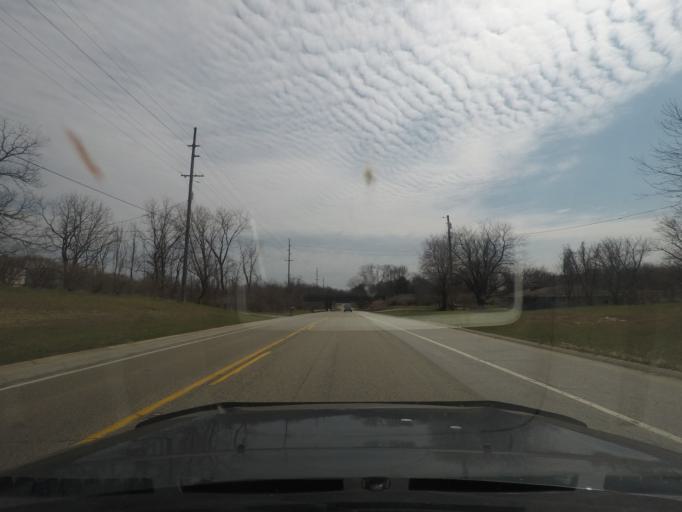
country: US
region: Indiana
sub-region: LaPorte County
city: LaPorte
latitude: 41.6561
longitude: -86.7645
